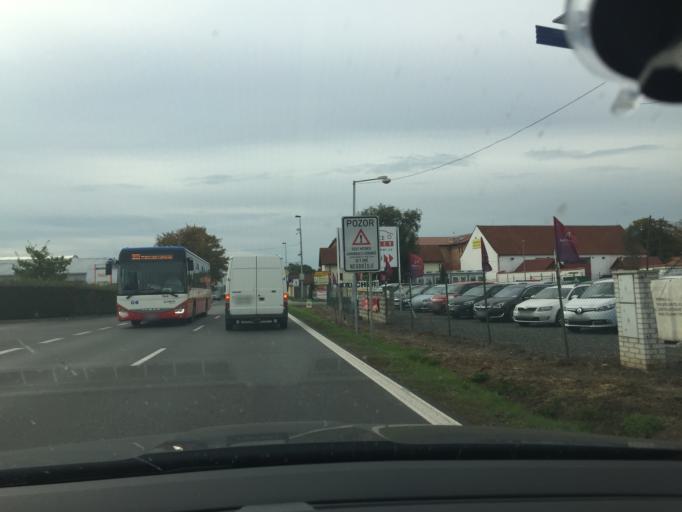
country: CZ
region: Praha
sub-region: Praha 20
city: Horni Pocernice
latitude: 50.1183
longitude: 14.6371
